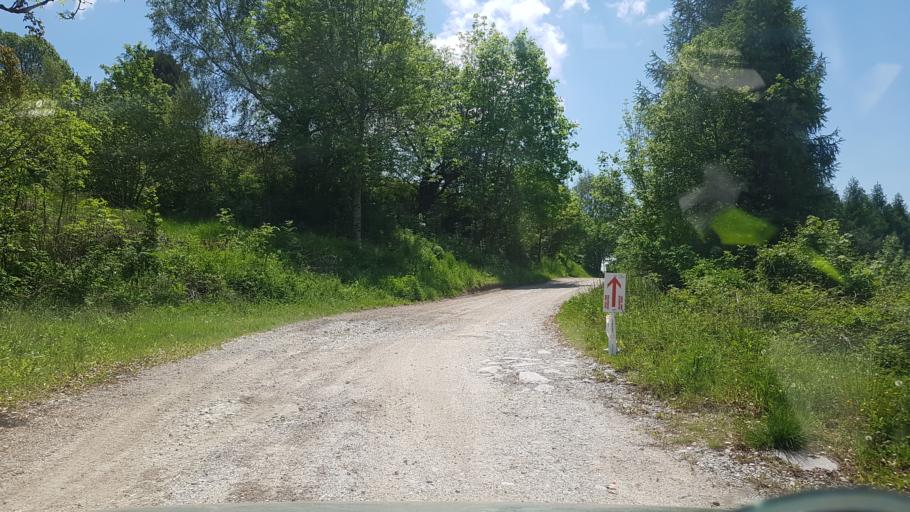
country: IT
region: Friuli Venezia Giulia
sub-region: Provincia di Udine
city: Pulfero
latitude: 46.1822
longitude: 13.4300
